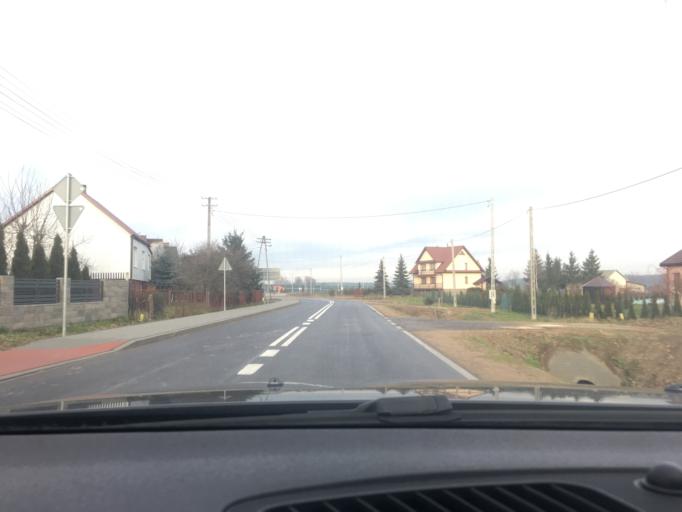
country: PL
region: Swietokrzyskie
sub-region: Powiat jedrzejowski
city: Jedrzejow
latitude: 50.6591
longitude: 20.3347
